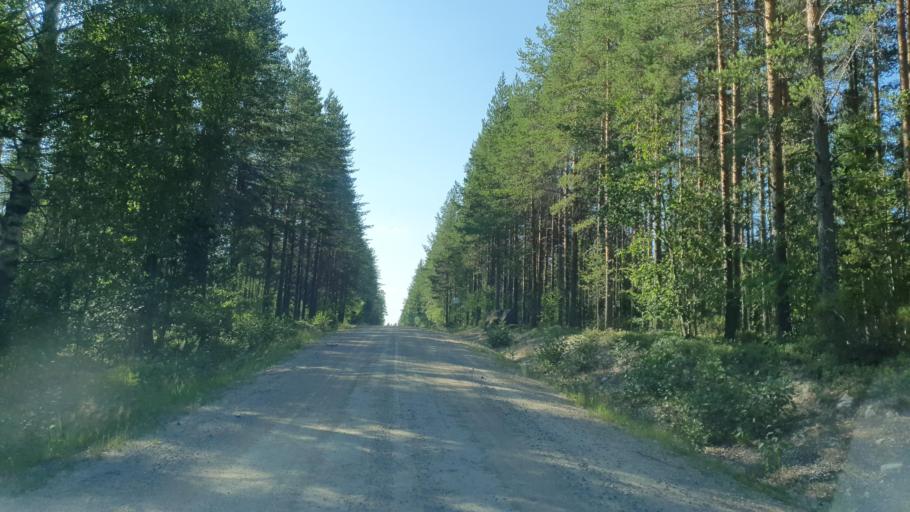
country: FI
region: Kainuu
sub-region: Kehys-Kainuu
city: Kuhmo
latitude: 64.0238
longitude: 29.7250
